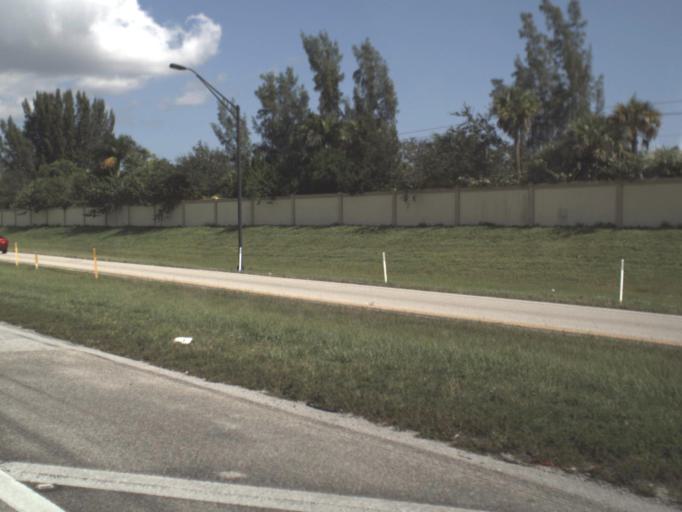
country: US
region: Florida
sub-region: Palm Beach County
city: Palm Beach Gardens
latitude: 26.7998
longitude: -80.1315
